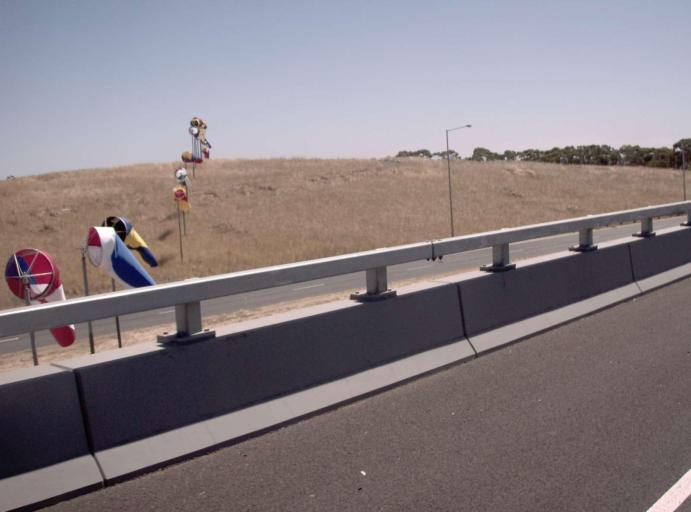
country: AU
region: Victoria
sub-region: Brimbank
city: Deer Park
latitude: -37.7702
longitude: 144.7952
